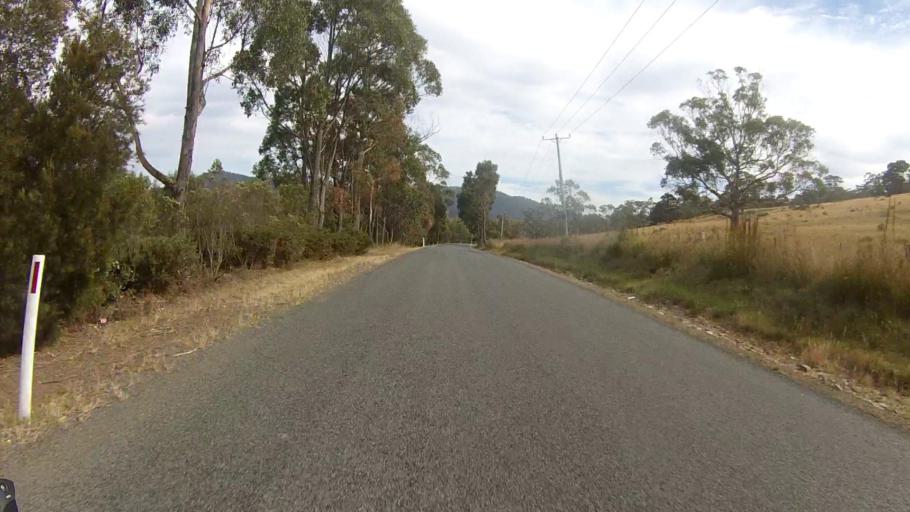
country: AU
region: Tasmania
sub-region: Sorell
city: Sorell
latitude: -42.8059
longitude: 147.7938
